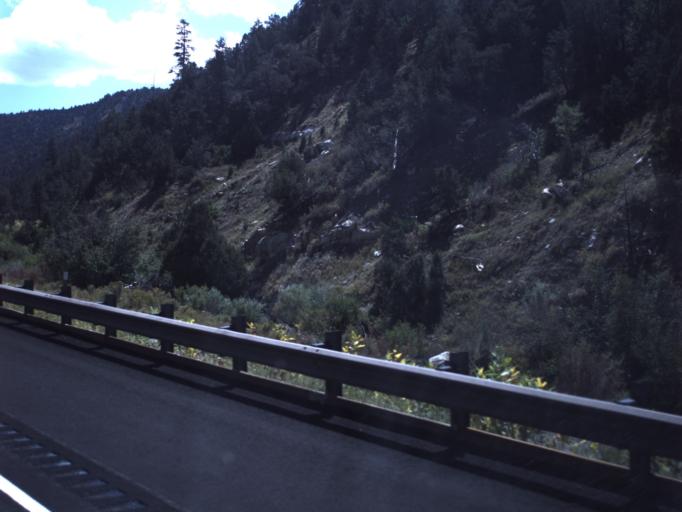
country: US
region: Utah
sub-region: Sevier County
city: Salina
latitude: 38.8924
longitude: -111.6182
